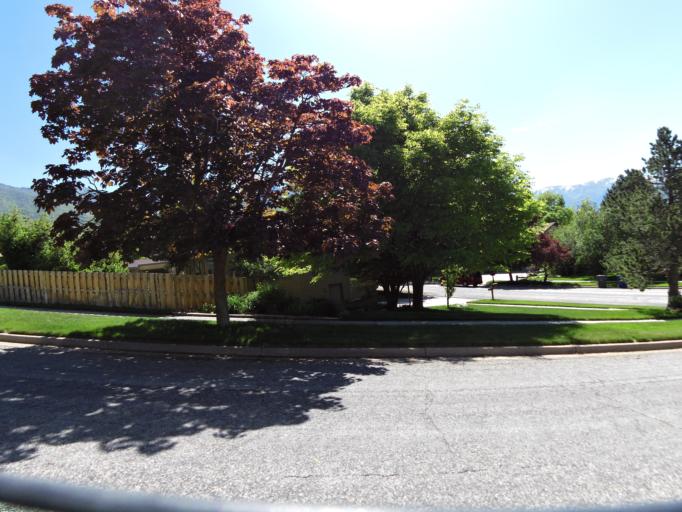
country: US
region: Utah
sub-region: Weber County
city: Uintah
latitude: 41.1704
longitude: -111.9380
